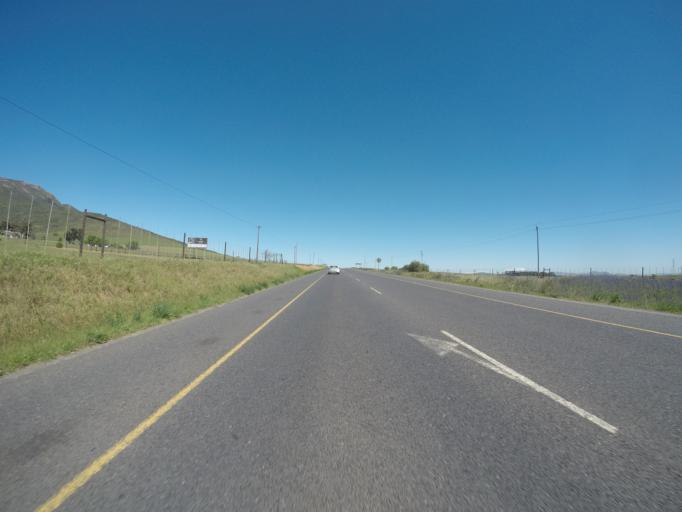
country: ZA
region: Western Cape
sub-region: Cape Winelands District Municipality
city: Noorder-Paarl
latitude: -33.6976
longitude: 18.8975
